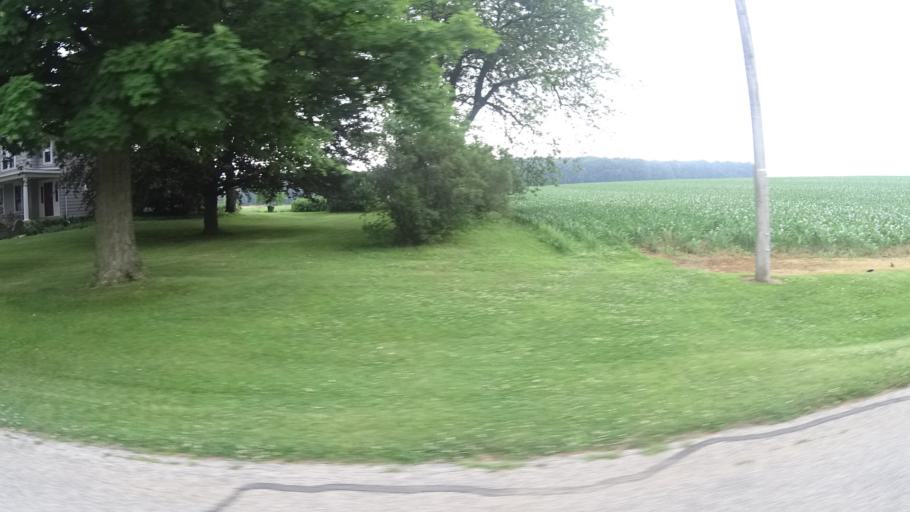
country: US
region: Ohio
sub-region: Erie County
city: Milan
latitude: 41.2898
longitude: -82.5118
